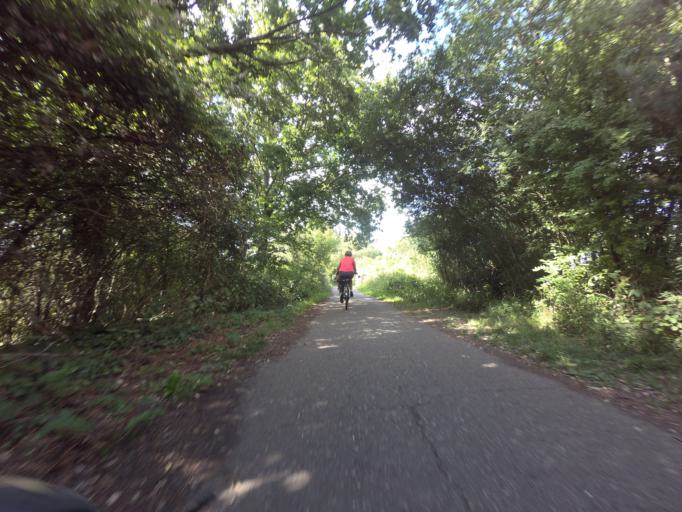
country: GB
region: England
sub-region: East Sussex
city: Hailsham
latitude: 50.8510
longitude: 0.2576
